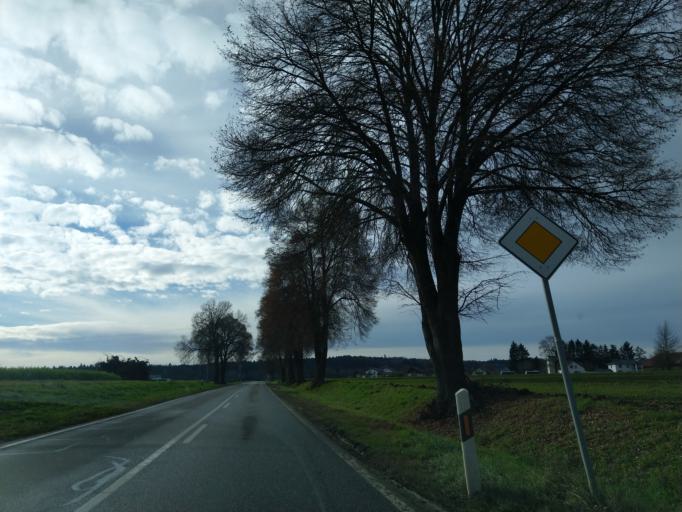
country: DE
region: Bavaria
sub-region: Lower Bavaria
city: Osterhofen
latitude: 48.6591
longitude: 12.9815
